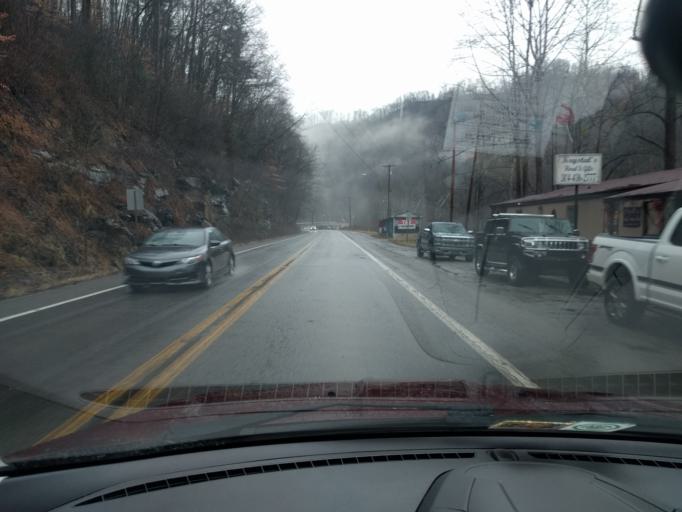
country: US
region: West Virginia
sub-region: McDowell County
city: Welch
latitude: 37.4298
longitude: -81.5609
